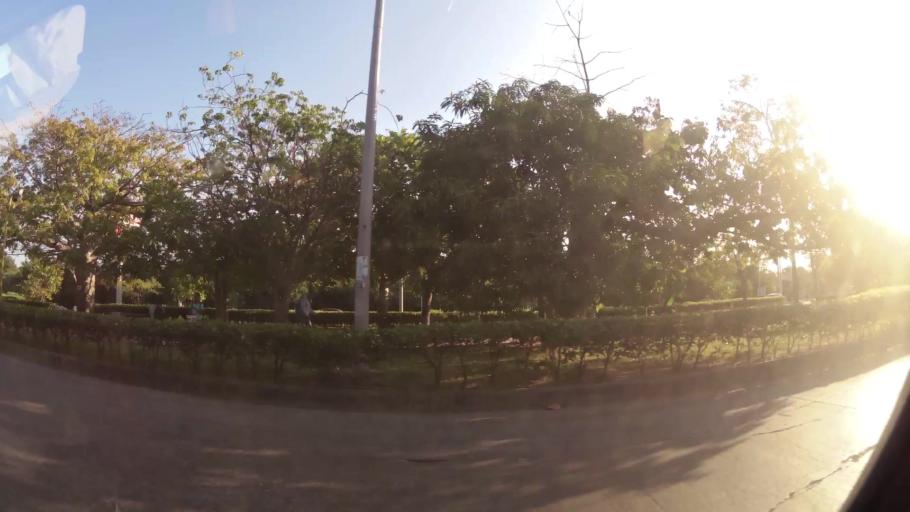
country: CO
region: Bolivar
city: Cartagena
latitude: 10.4430
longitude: -75.5233
